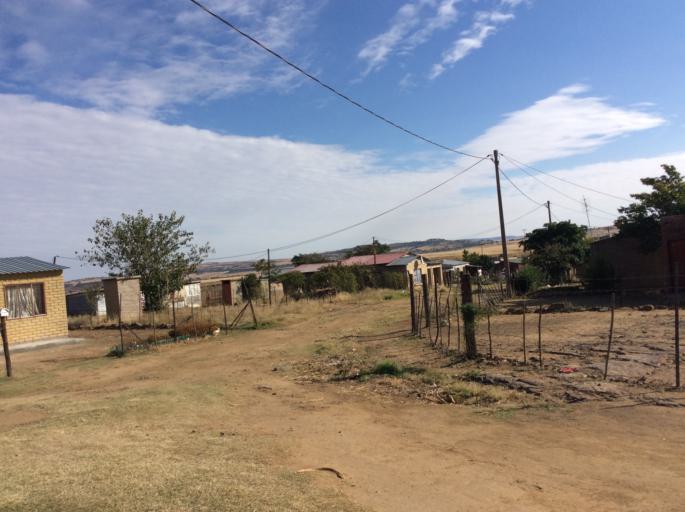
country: LS
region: Mafeteng
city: Mafeteng
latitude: -29.7194
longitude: 27.0121
